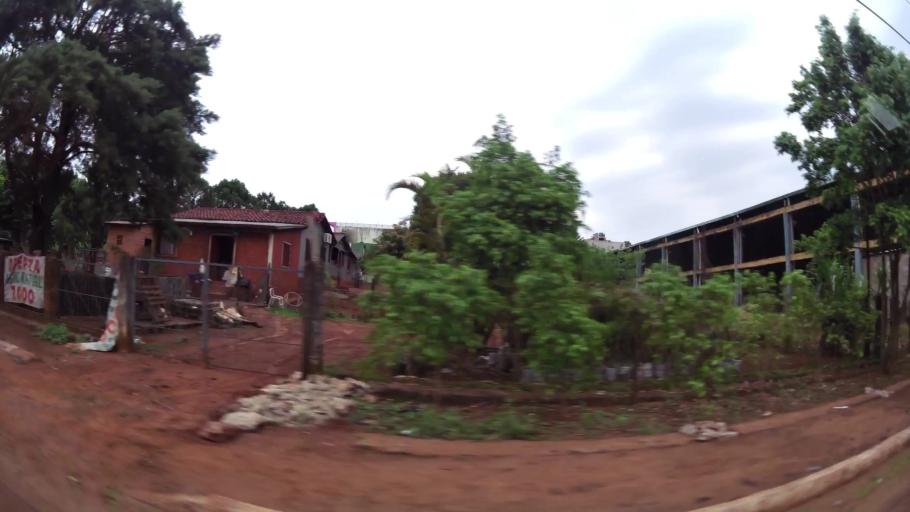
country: PY
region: Alto Parana
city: Presidente Franco
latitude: -25.5238
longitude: -54.6457
